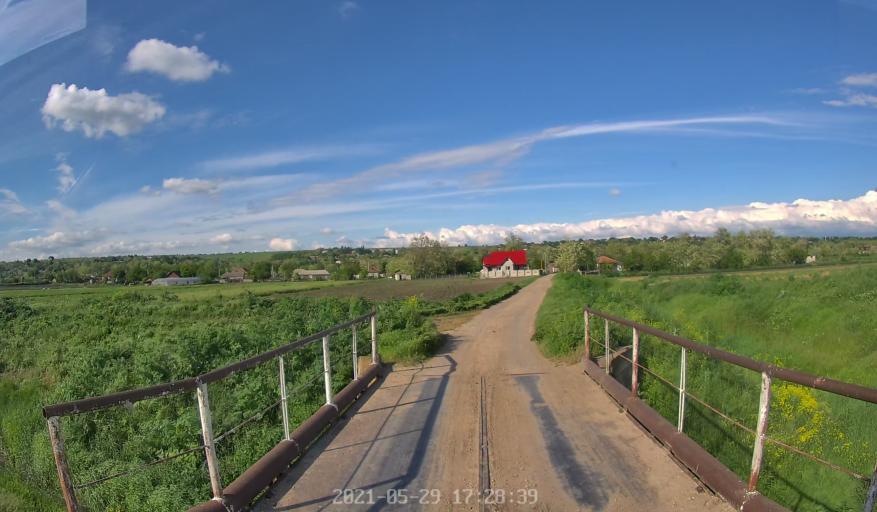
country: MD
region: Laloveni
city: Ialoveni
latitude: 46.8339
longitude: 28.8414
